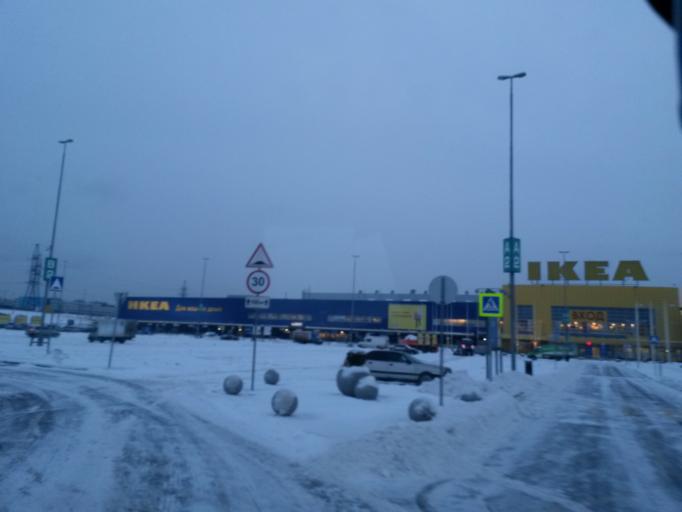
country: RU
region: Moscow
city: Tyoply Stan
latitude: 55.6047
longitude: 37.4929
